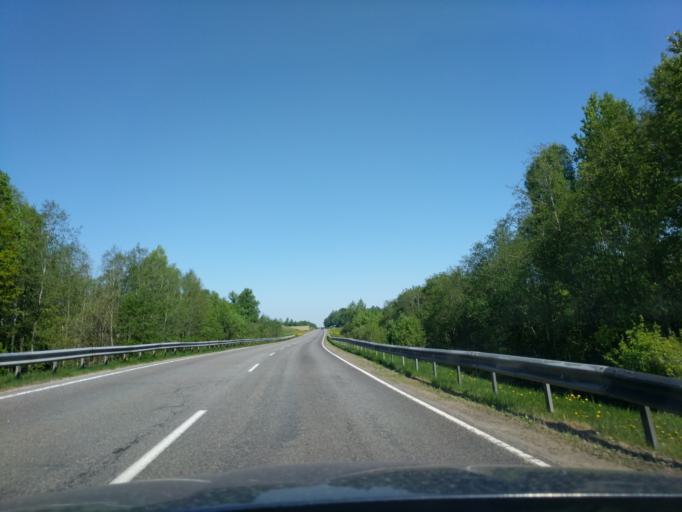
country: BY
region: Minsk
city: Il'ya
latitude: 54.3055
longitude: 27.4743
